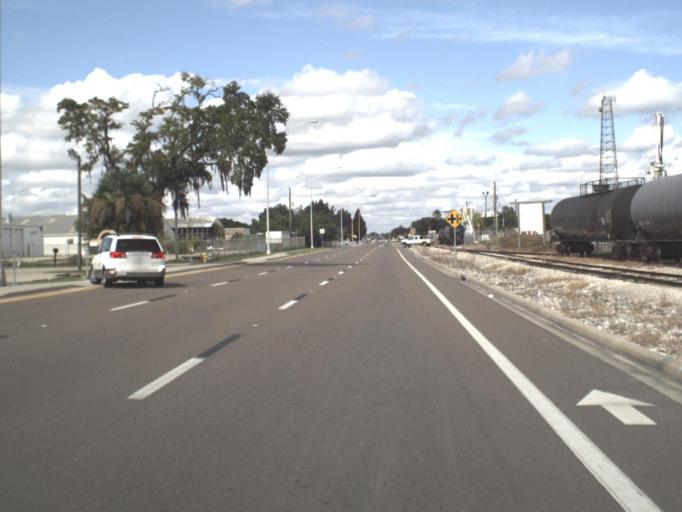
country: US
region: Florida
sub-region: Lee County
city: Fort Myers
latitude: 26.6274
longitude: -81.8601
